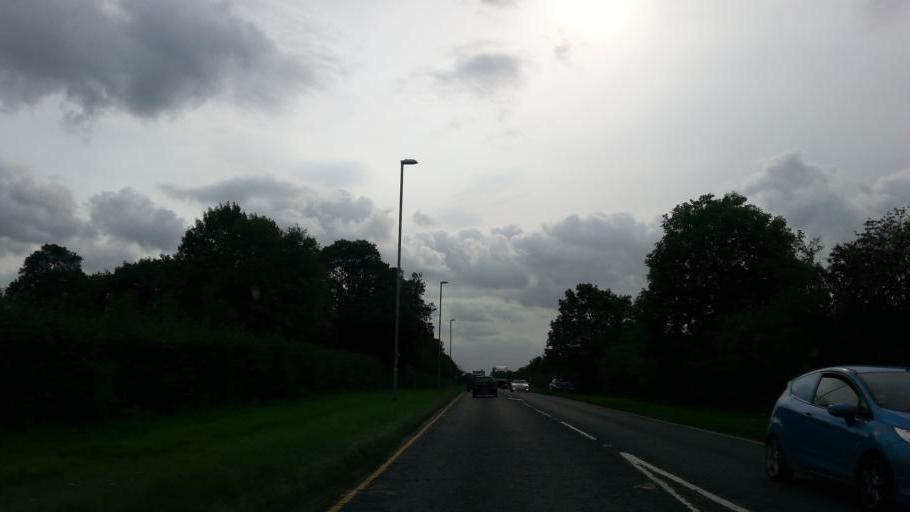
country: GB
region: England
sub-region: Cambridgeshire
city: Duxford
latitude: 52.0925
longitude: 0.1228
